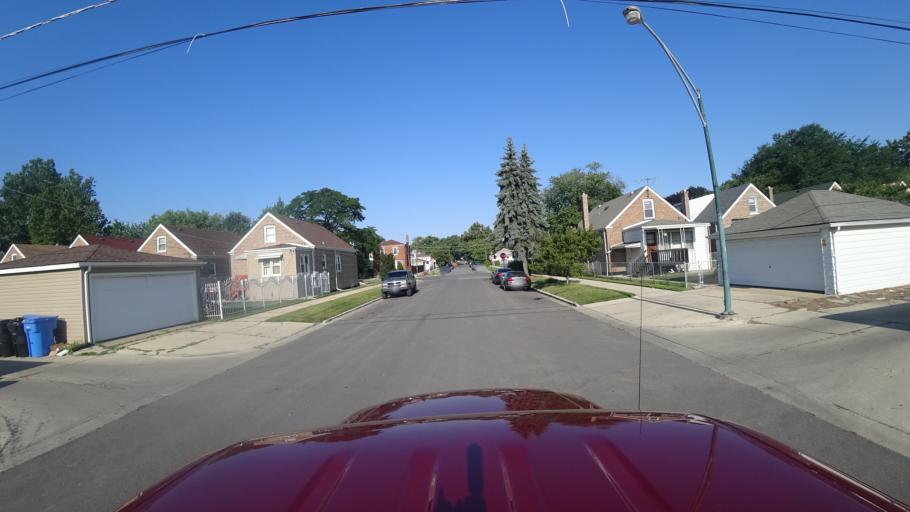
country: US
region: Illinois
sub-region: Cook County
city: Cicero
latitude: 41.7970
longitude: -87.7152
